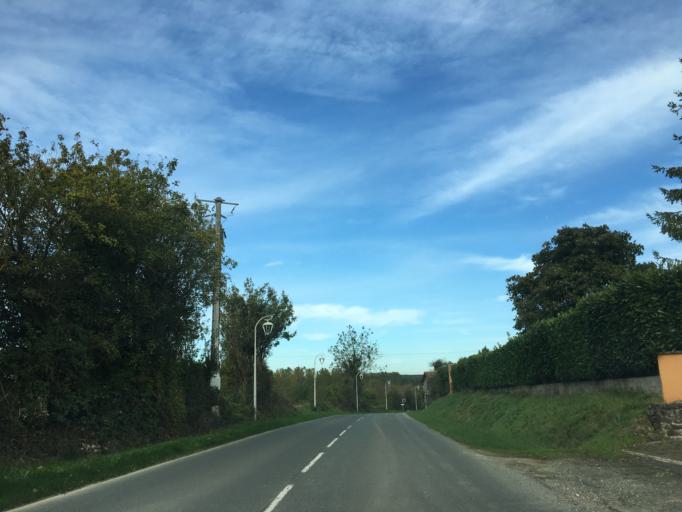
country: FR
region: Poitou-Charentes
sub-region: Departement de la Charente-Maritime
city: Aulnay
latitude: 46.0630
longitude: -0.4132
